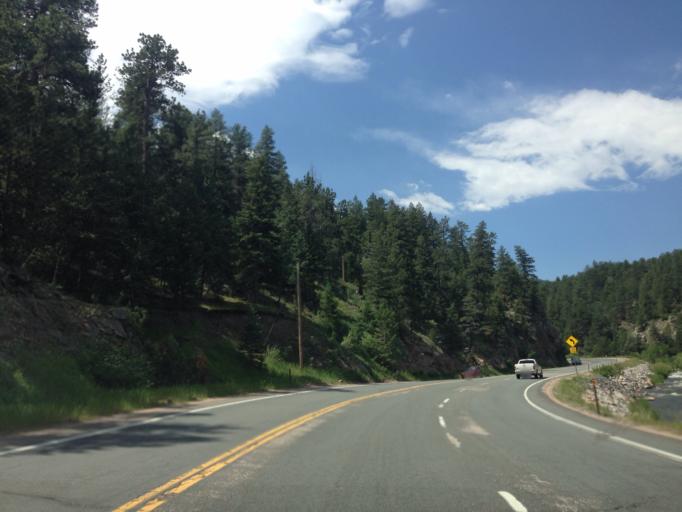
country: US
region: Colorado
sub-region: Larimer County
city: Estes Park
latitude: 40.4003
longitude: -105.4183
